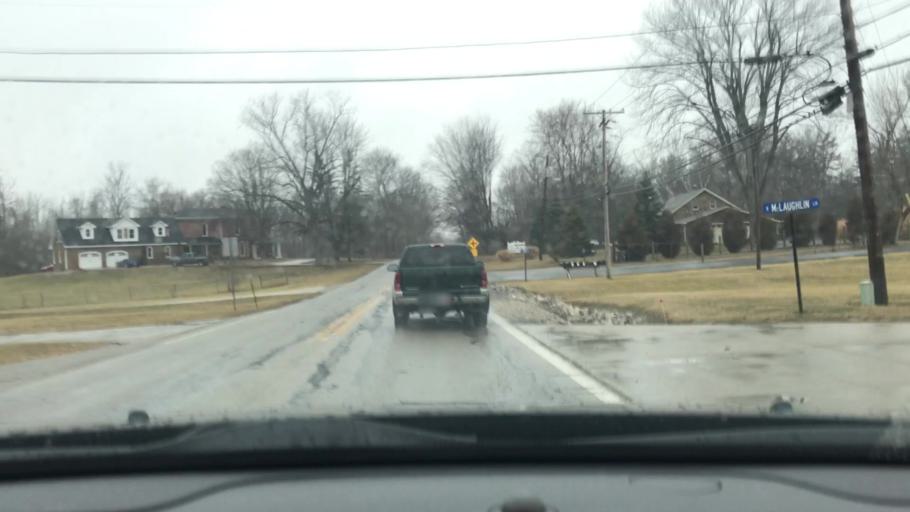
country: US
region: Indiana
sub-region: Morgan County
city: Mooresville
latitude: 39.5906
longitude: -86.3362
